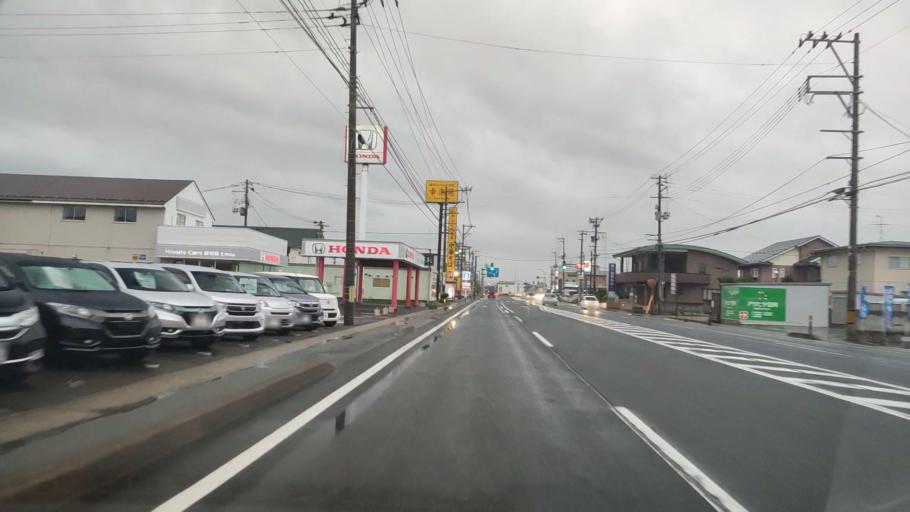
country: JP
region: Akita
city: Akita
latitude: 39.6870
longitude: 140.1247
